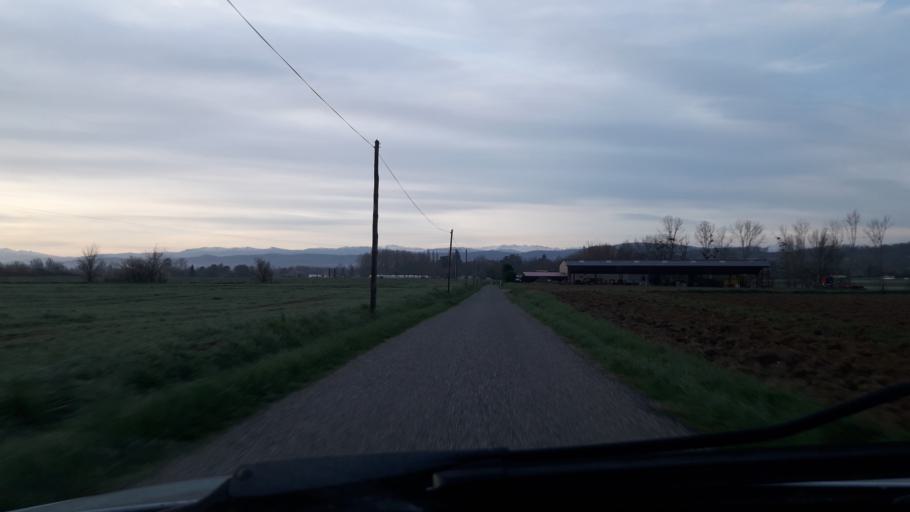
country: FR
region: Midi-Pyrenees
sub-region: Departement de la Haute-Garonne
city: Montesquieu-Volvestre
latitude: 43.1762
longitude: 1.2684
